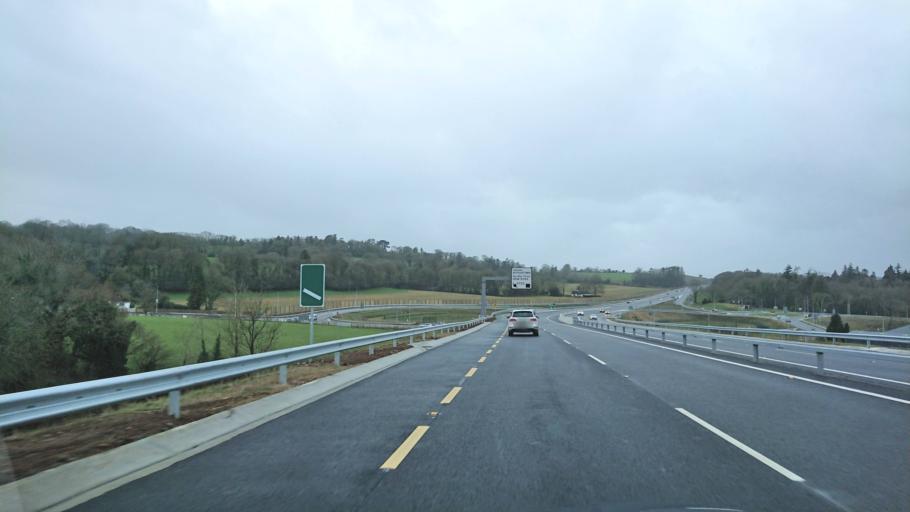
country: IE
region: Leinster
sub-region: Loch Garman
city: New Ross
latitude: 52.3637
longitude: -6.9564
